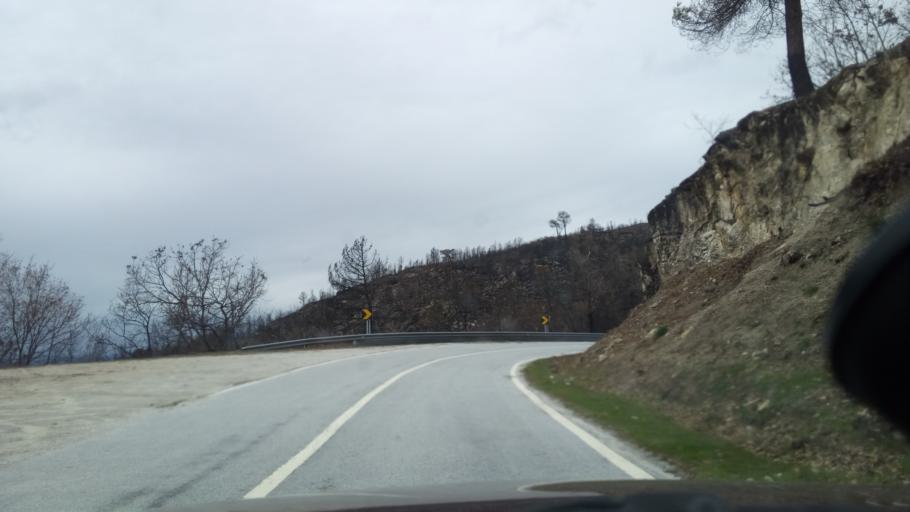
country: PT
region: Guarda
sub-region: Manteigas
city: Manteigas
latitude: 40.4682
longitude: -7.5876
